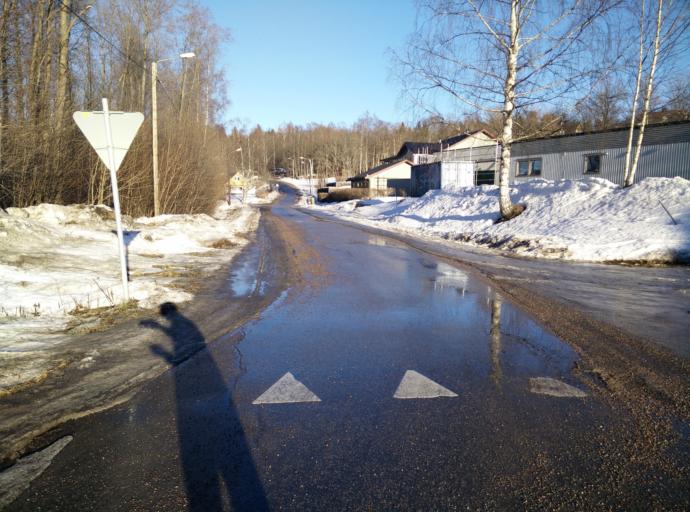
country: SE
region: Vaesternorrland
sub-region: Sundsvalls Kommun
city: Skottsund
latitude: 62.3105
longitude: 17.3911
